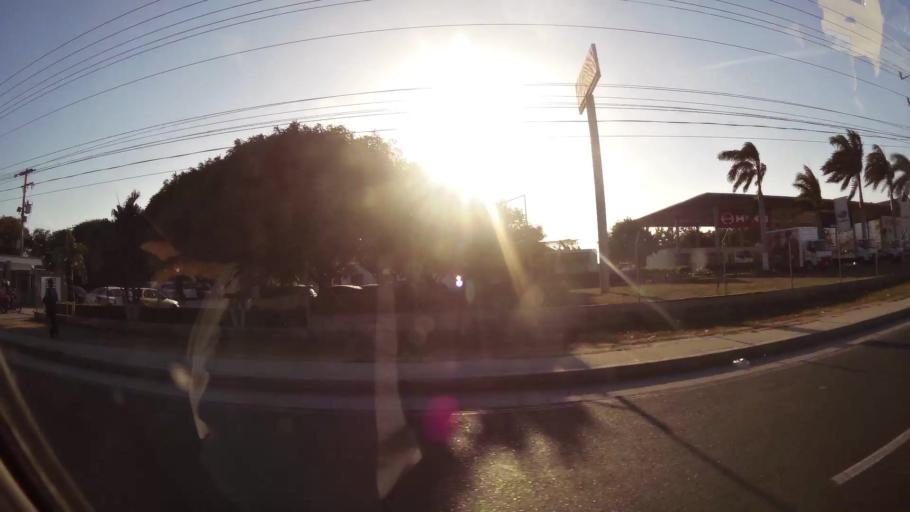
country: CO
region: Atlantico
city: Soledad
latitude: 10.9210
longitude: -74.7764
